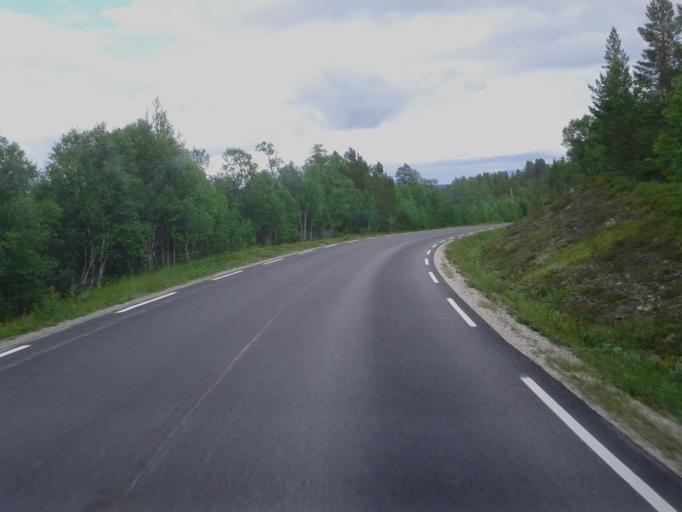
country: NO
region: Sor-Trondelag
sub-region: Roros
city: Roros
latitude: 62.3091
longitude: 11.6841
